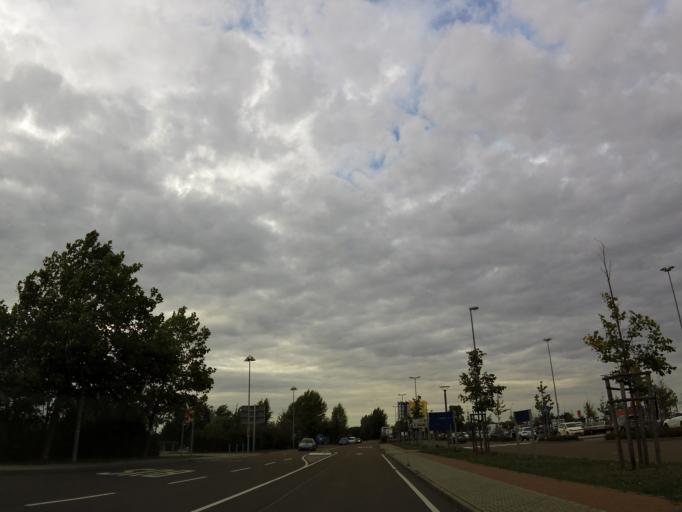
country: DE
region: Saxony-Anhalt
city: Gunthersdorf
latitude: 51.3480
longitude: 12.1805
